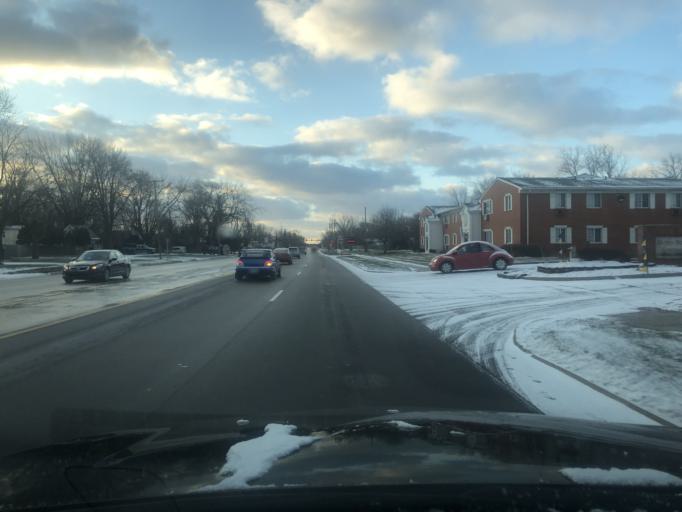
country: US
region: Michigan
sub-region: Wayne County
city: Wayne
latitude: 42.2560
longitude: -83.3480
